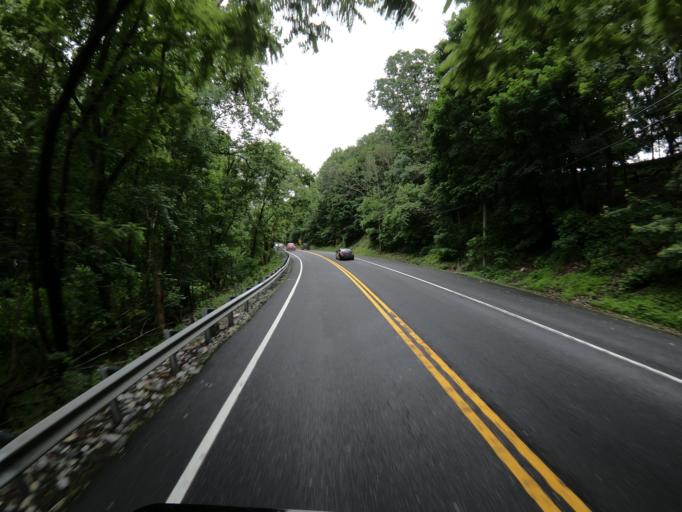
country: US
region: Maryland
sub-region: Washington County
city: Boonsboro
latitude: 39.4900
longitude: -77.6346
